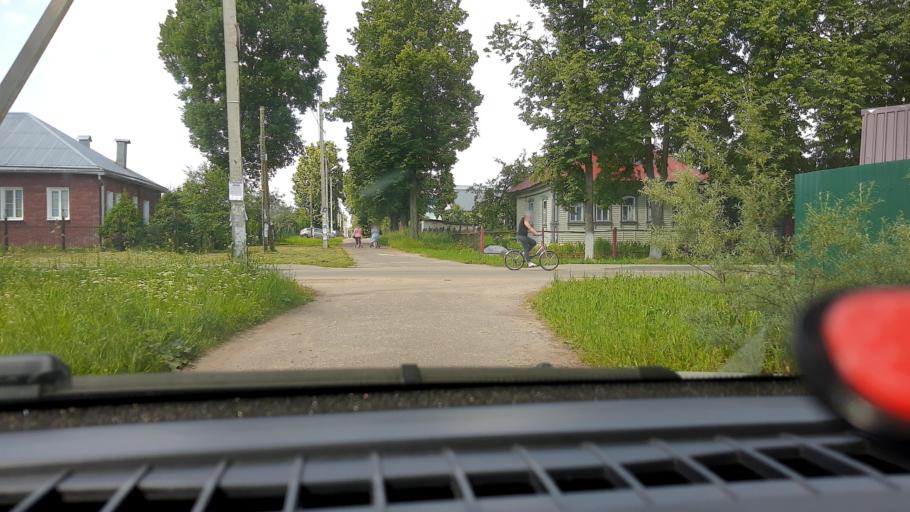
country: RU
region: Nizjnij Novgorod
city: Gorbatovka
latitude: 56.2676
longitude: 43.7561
